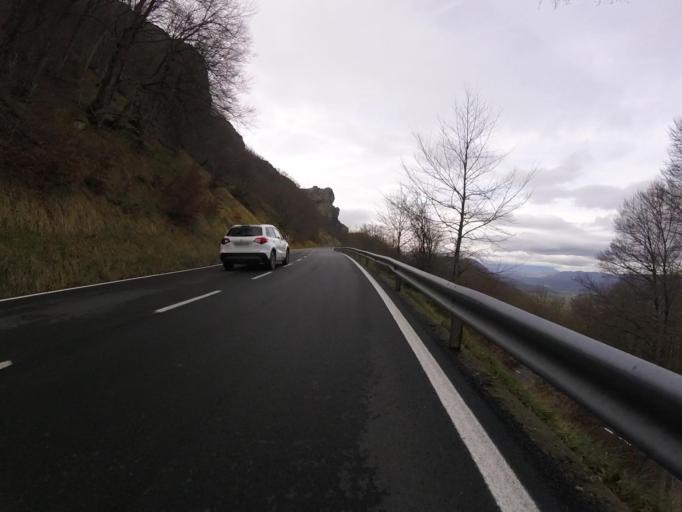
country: ES
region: Navarre
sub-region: Provincia de Navarra
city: Arruazu
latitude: 42.8639
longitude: -1.9979
